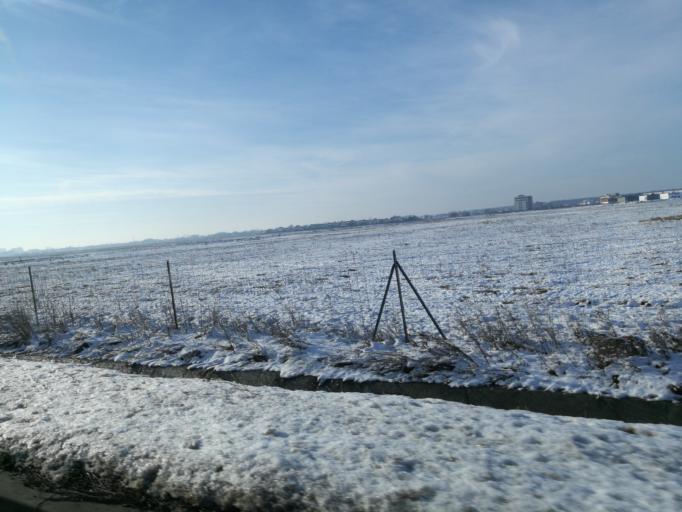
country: RO
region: Ilfov
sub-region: Voluntari City
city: Voluntari
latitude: 44.5113
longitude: 26.1650
